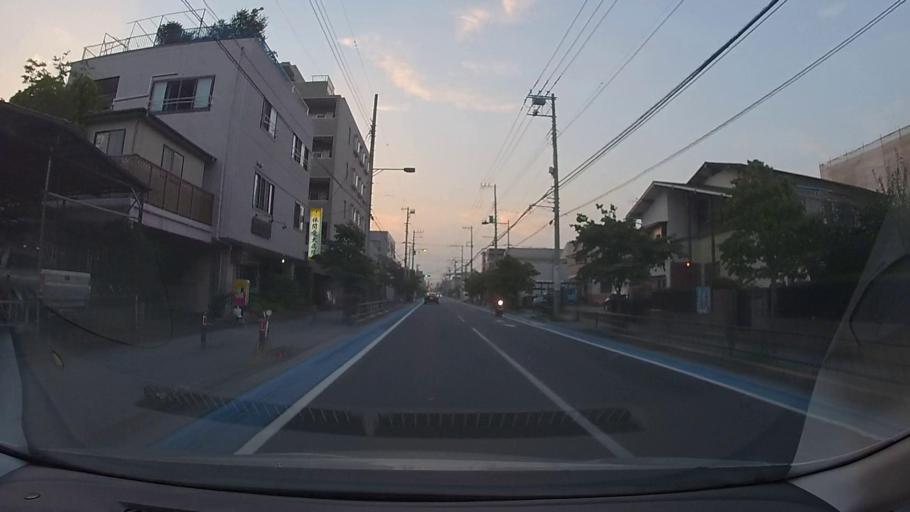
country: JP
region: Kanagawa
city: Minami-rinkan
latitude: 35.4907
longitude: 139.4472
